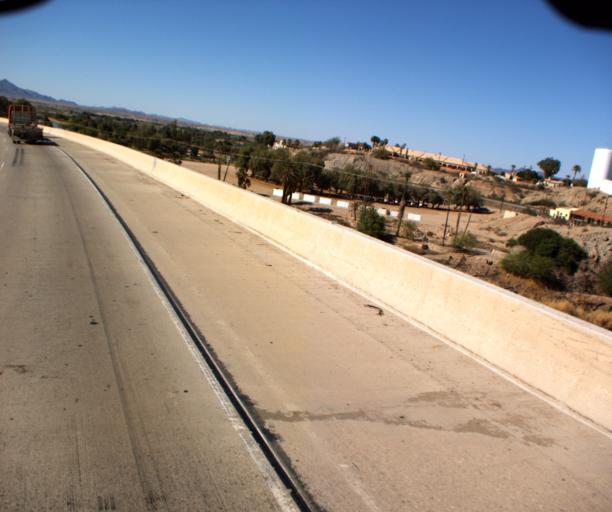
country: US
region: Arizona
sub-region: Yuma County
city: Yuma
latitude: 32.7277
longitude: -114.6166
